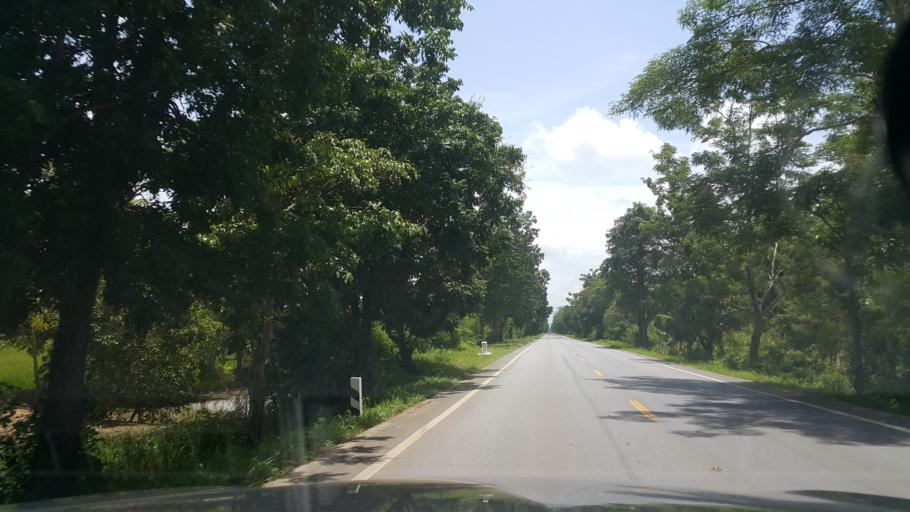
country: TH
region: Sukhothai
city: Sawankhalok
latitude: 17.3291
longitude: 99.7391
